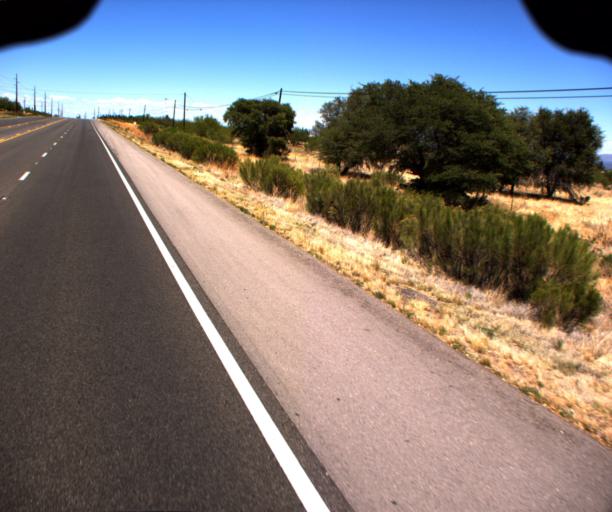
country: US
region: Arizona
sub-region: Cochise County
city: Sierra Vista Southeast
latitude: 31.4190
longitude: -110.2407
